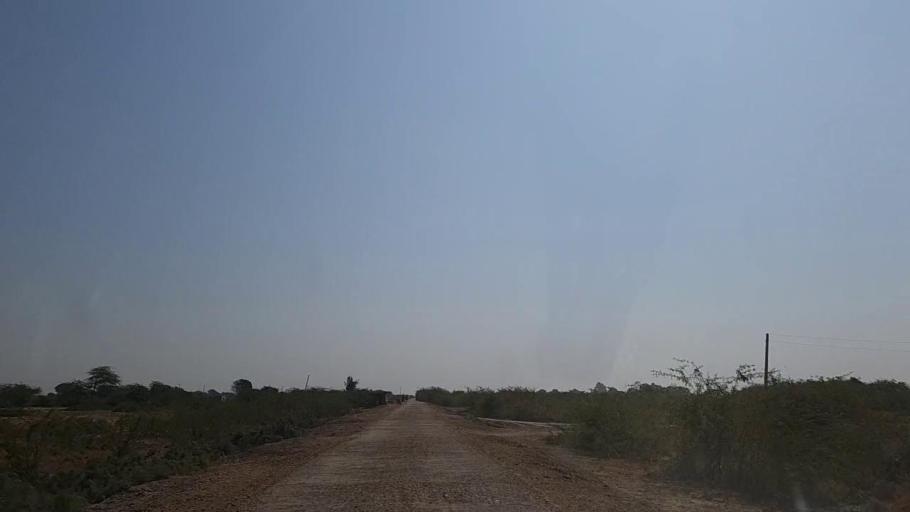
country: PK
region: Sindh
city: Digri
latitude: 24.9803
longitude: 69.2037
